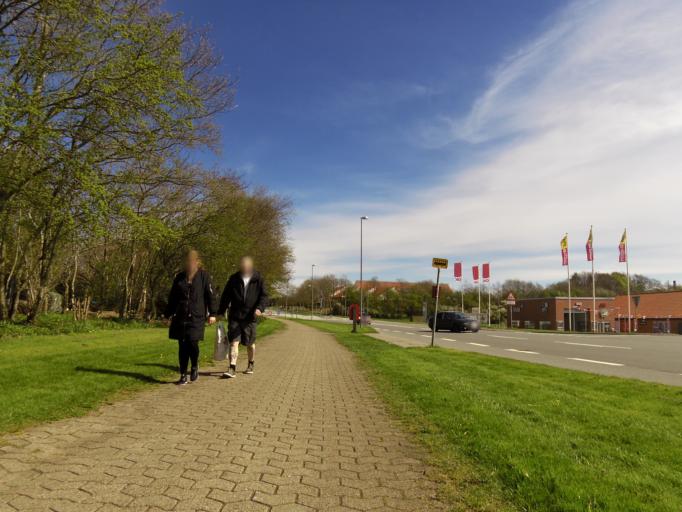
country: DK
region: Central Jutland
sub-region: Skive Kommune
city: Skive
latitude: 56.5858
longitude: 9.0272
